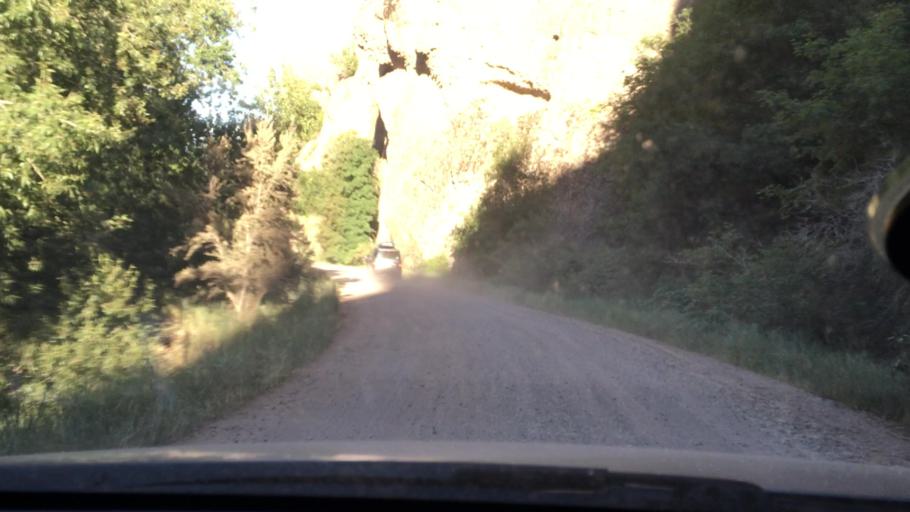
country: US
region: Utah
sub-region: Sanpete County
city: Fountain Green
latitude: 39.5551
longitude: -111.6722
